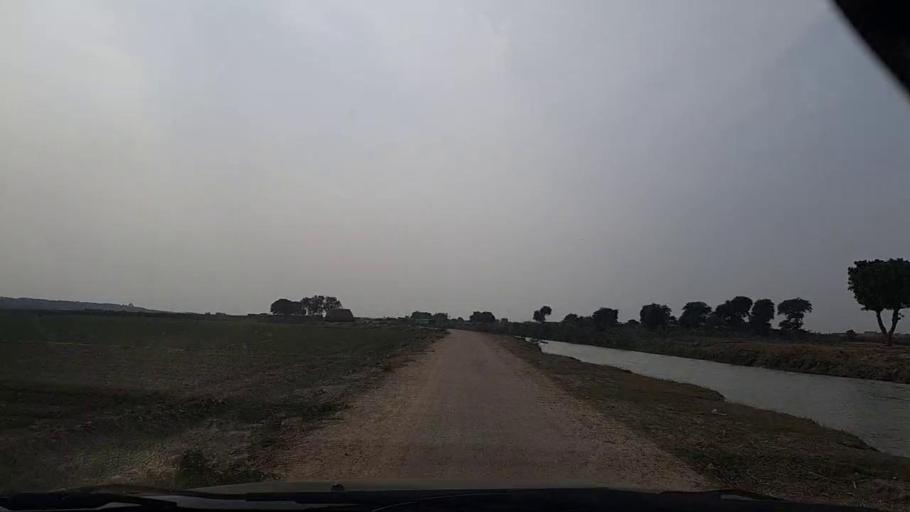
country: PK
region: Sindh
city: Thatta
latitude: 24.5758
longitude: 67.8815
